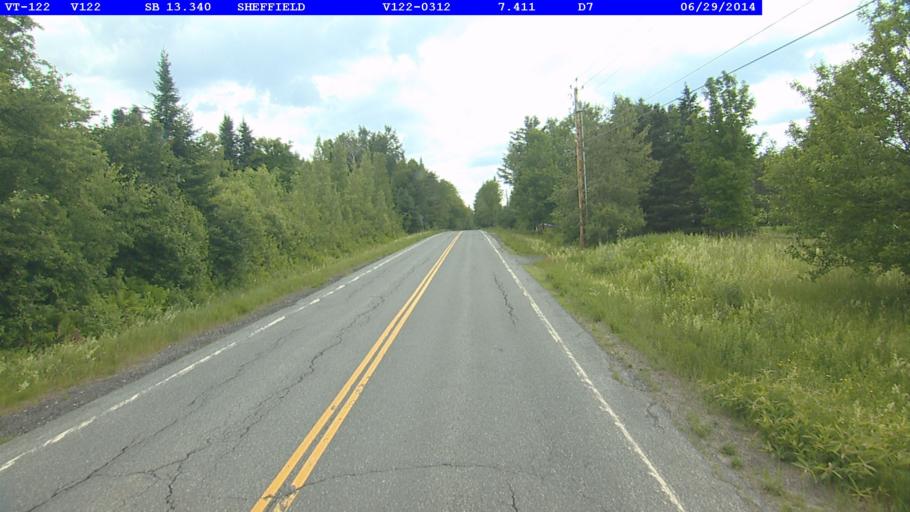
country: US
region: Vermont
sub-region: Caledonia County
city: Lyndonville
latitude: 44.6749
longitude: -72.1610
